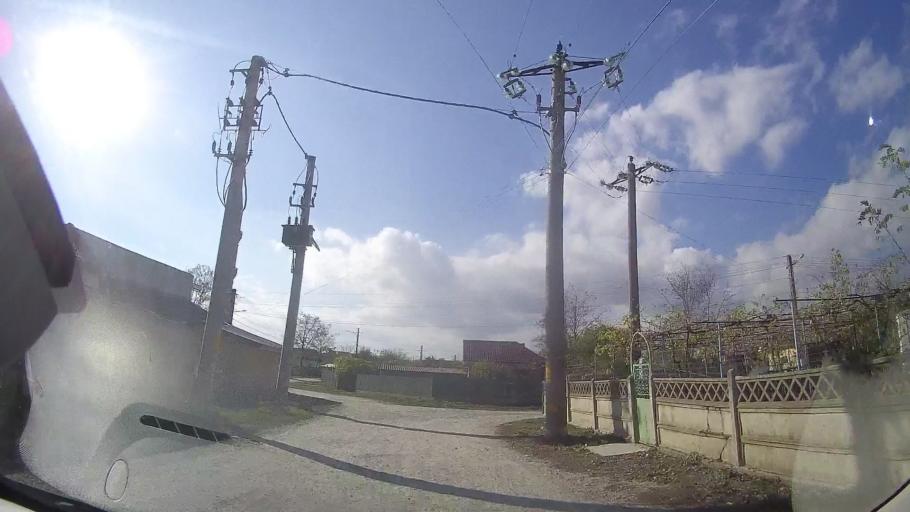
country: RO
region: Constanta
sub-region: Comuna Douazeci si Trei August
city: Douazeci si Trei August
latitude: 43.9150
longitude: 28.5845
